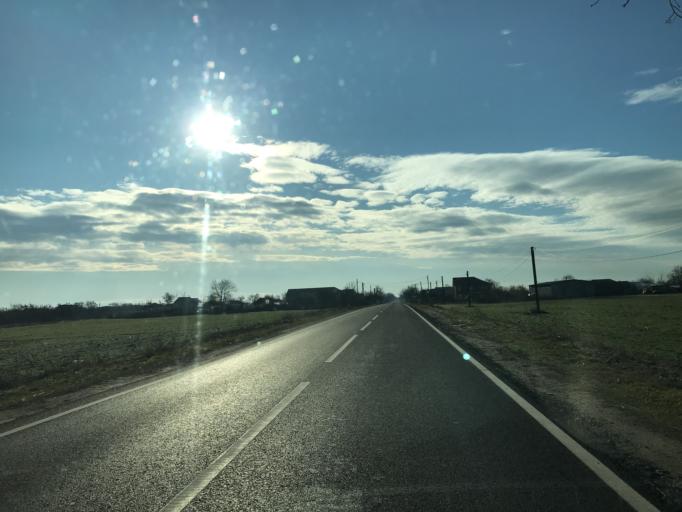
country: RO
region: Olt
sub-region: Comuna Ganeasa
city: Ganeasa
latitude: 44.3922
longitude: 24.2809
